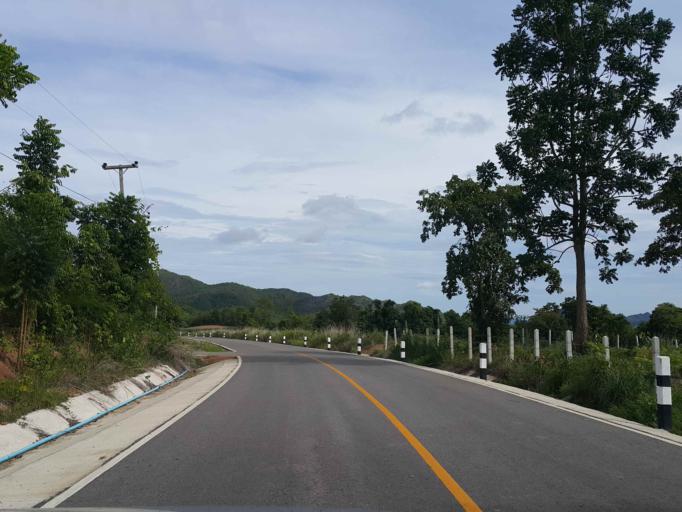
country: TH
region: Sukhothai
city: Thung Saliam
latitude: 17.2353
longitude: 99.5075
